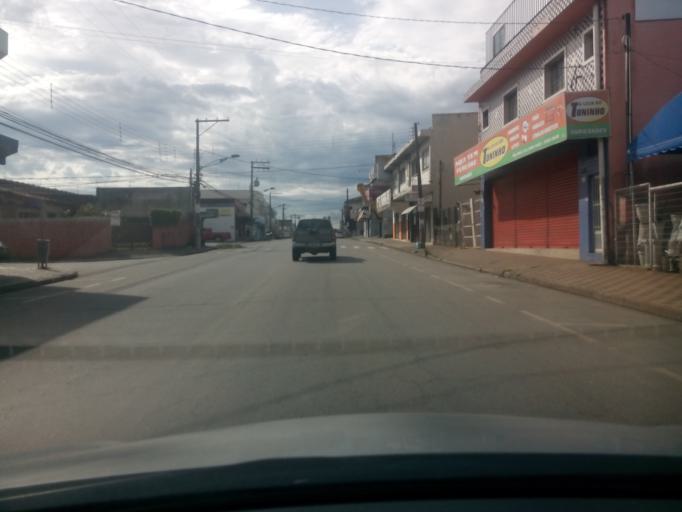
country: BR
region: Sao Paulo
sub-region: Peruibe
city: Peruibe
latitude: -24.3207
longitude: -47.0040
